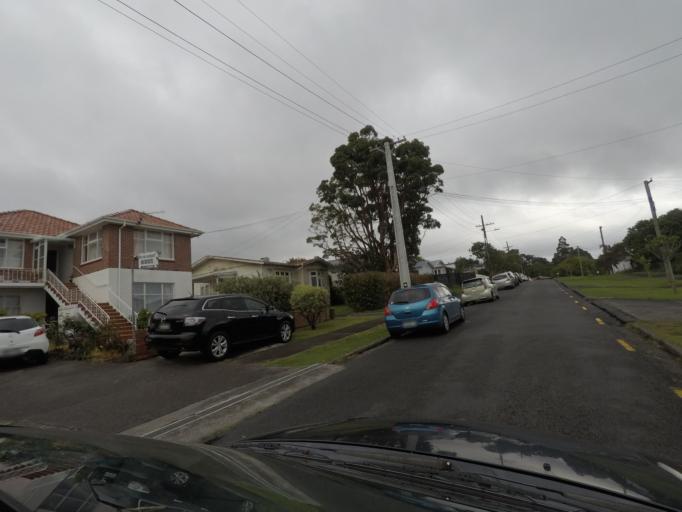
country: NZ
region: Auckland
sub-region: Auckland
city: Auckland
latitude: -36.8925
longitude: 174.7303
